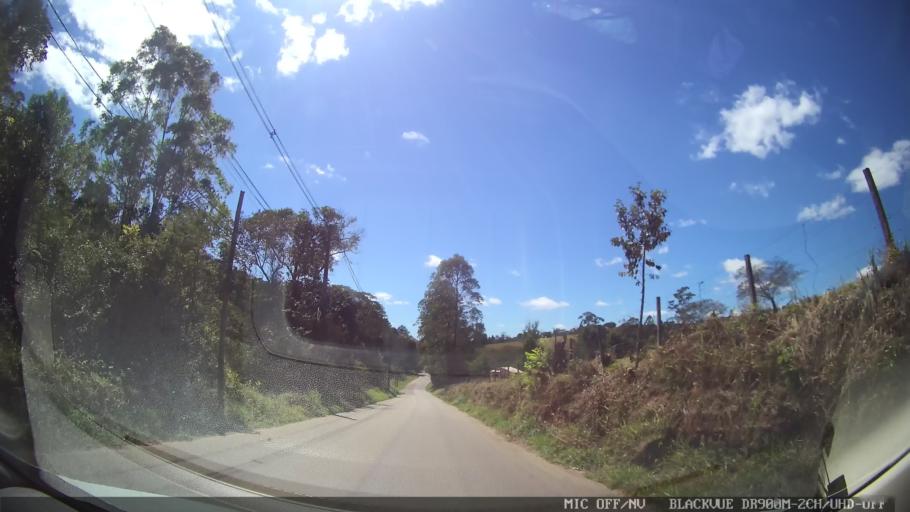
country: BR
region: Sao Paulo
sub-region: Campo Limpo Paulista
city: Campo Limpo Paulista
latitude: -23.1695
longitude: -46.7347
